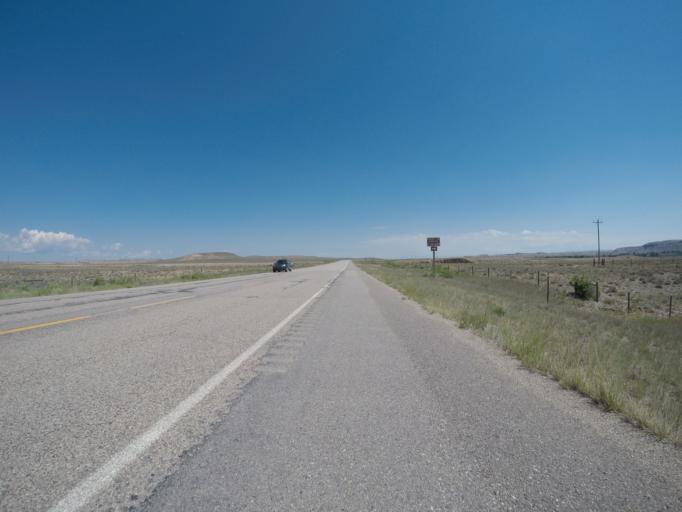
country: US
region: Wyoming
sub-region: Sublette County
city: Marbleton
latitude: 42.4230
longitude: -110.1112
